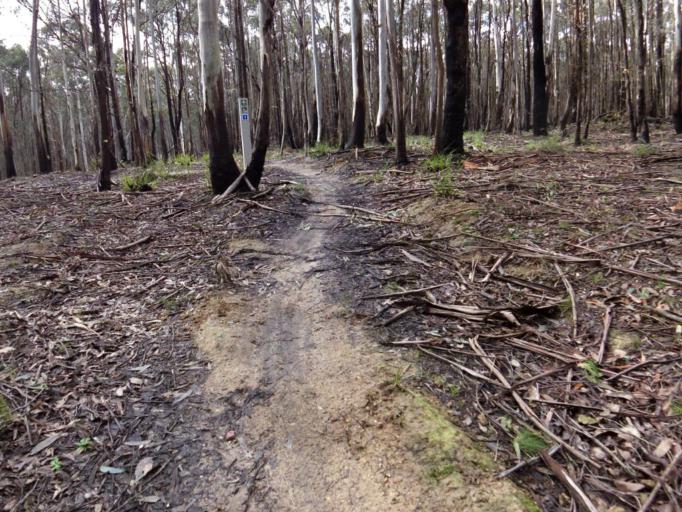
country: AU
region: Victoria
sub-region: Moorabool
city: Bacchus Marsh
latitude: -37.4234
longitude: 144.4878
